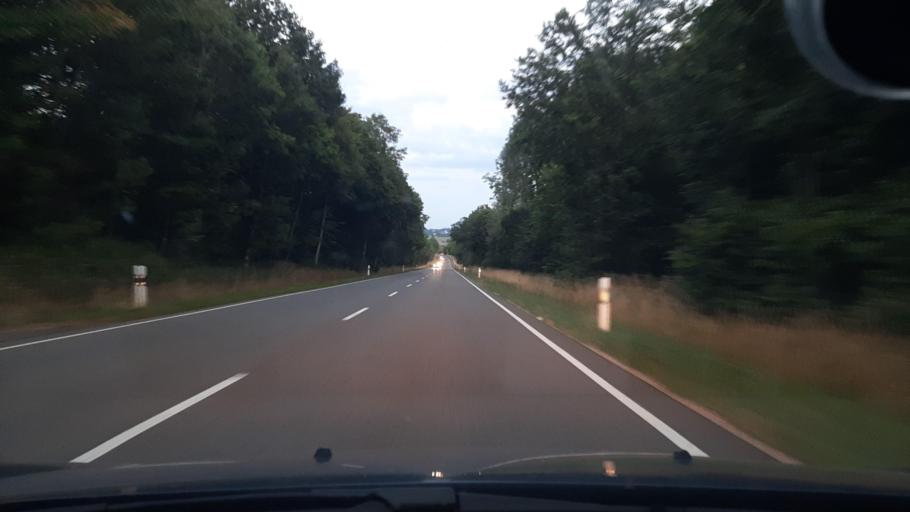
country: DE
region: North Rhine-Westphalia
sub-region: Regierungsbezirk Koln
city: Nettersheim
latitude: 50.4480
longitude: 6.5804
